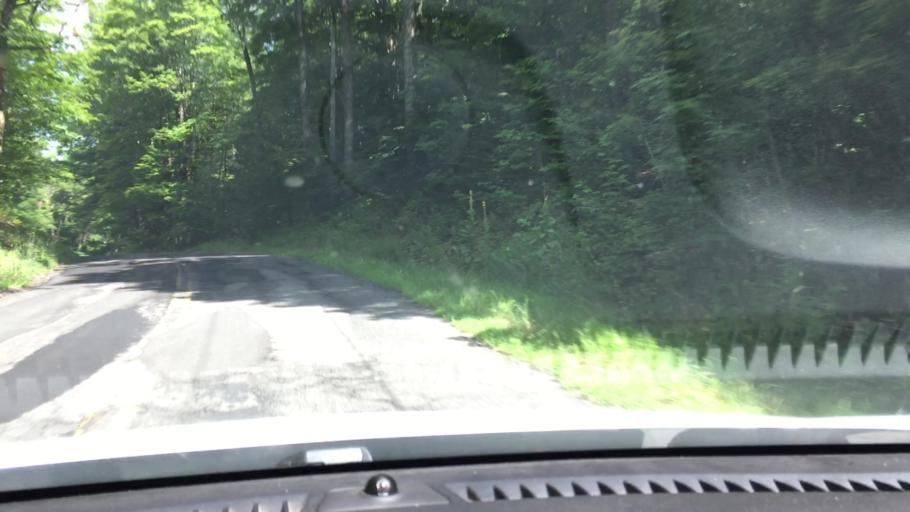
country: US
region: Massachusetts
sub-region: Berkshire County
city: Otis
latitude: 42.1939
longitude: -73.1589
